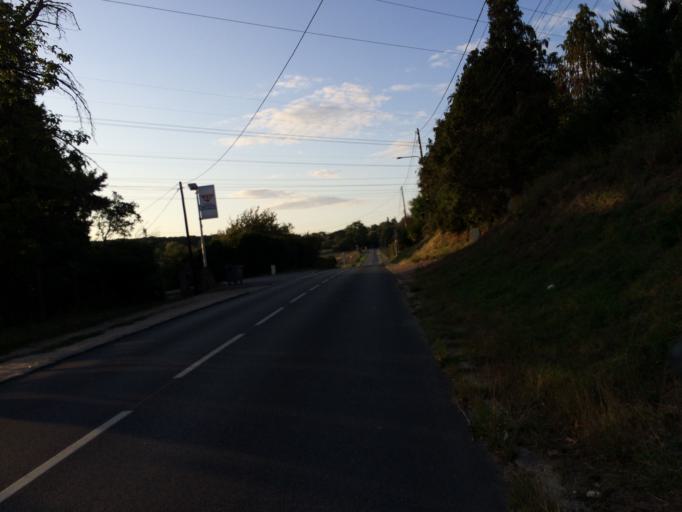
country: FR
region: Ile-de-France
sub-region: Departement de l'Essonne
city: Nozay
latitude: 48.6576
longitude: 2.2086
